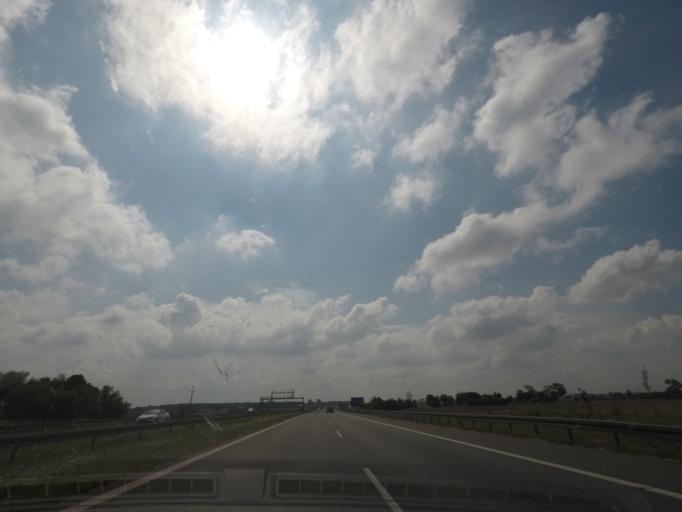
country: PL
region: Lodz Voivodeship
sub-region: Powiat kutnowski
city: Krzyzanow
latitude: 52.2082
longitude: 19.4816
